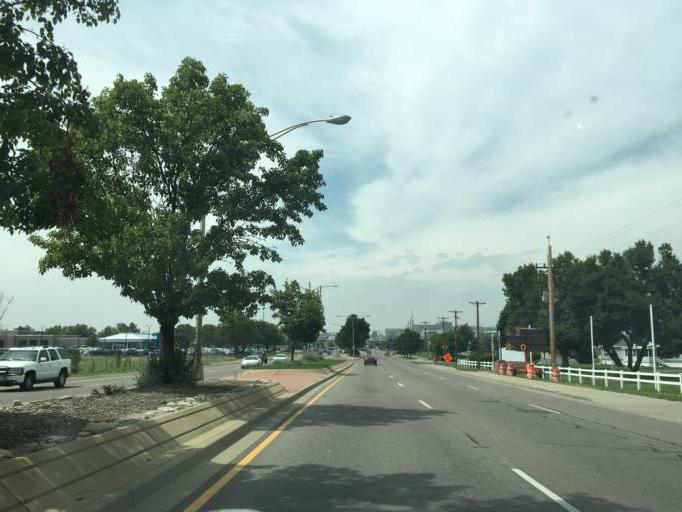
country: US
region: Colorado
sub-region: Adams County
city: Aurora
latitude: 39.7401
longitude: -104.8154
